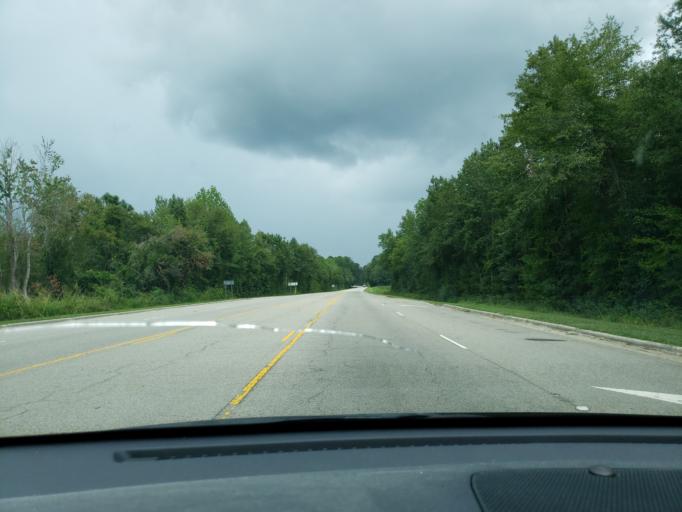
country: US
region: North Carolina
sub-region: Bladen County
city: Bladenboro
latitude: 34.4960
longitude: -78.6586
